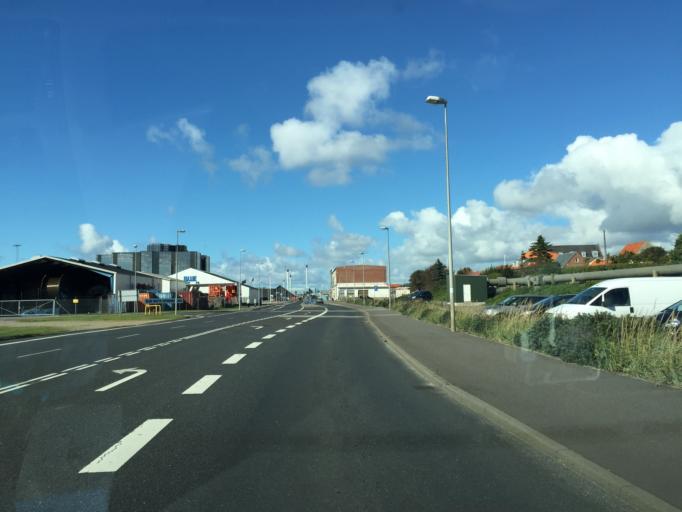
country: DK
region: South Denmark
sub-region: Esbjerg Kommune
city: Esbjerg
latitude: 55.4672
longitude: 8.4379
